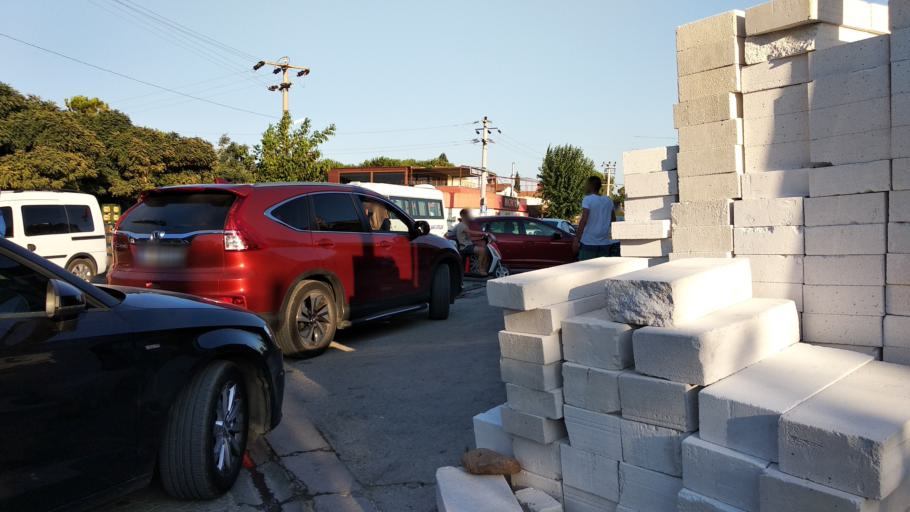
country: TR
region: Balikesir
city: Altinova
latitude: 39.1585
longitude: 26.8223
